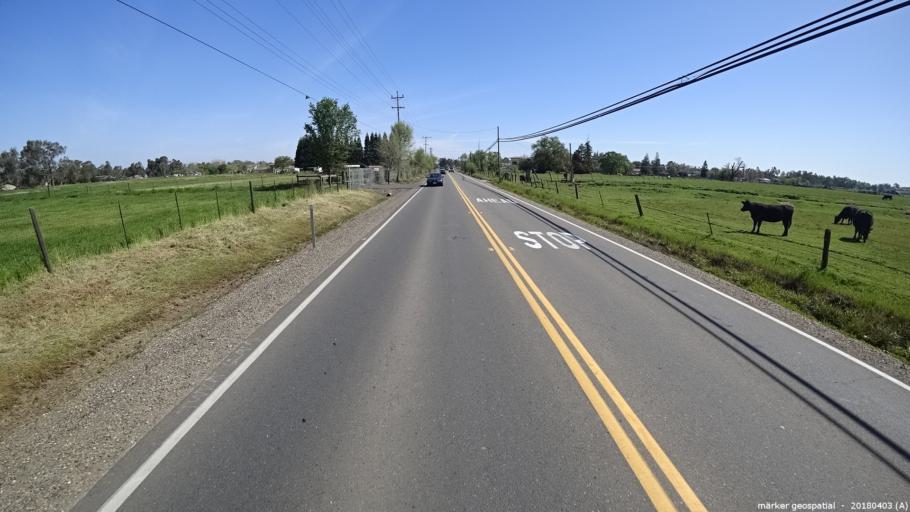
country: US
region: California
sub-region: Sacramento County
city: Wilton
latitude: 38.4032
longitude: -121.2540
